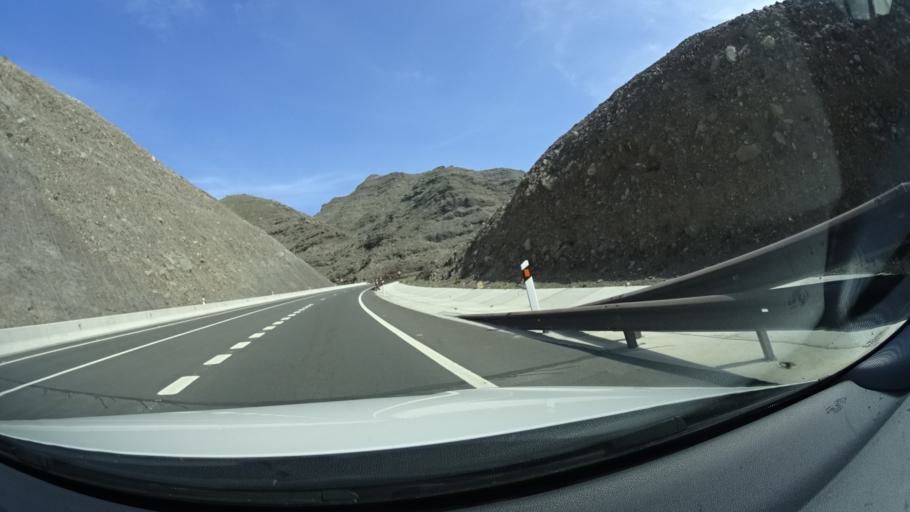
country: ES
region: Canary Islands
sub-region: Provincia de Las Palmas
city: San Nicolas
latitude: 28.0173
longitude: -15.7710
